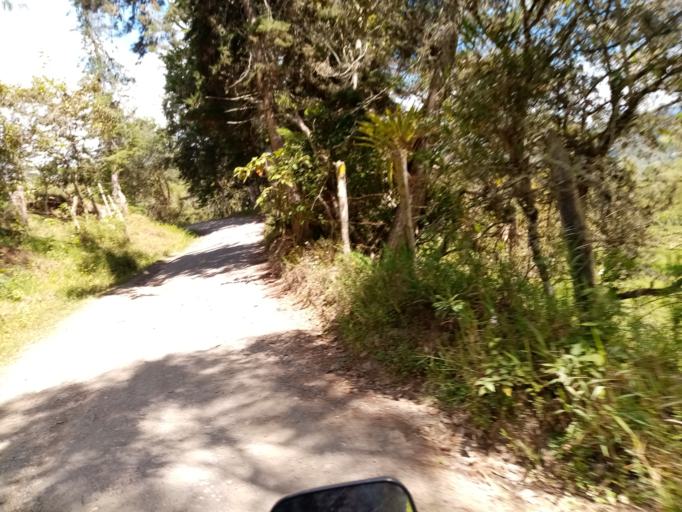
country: CO
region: Cundinamarca
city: Tenza
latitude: 5.0774
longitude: -73.4397
